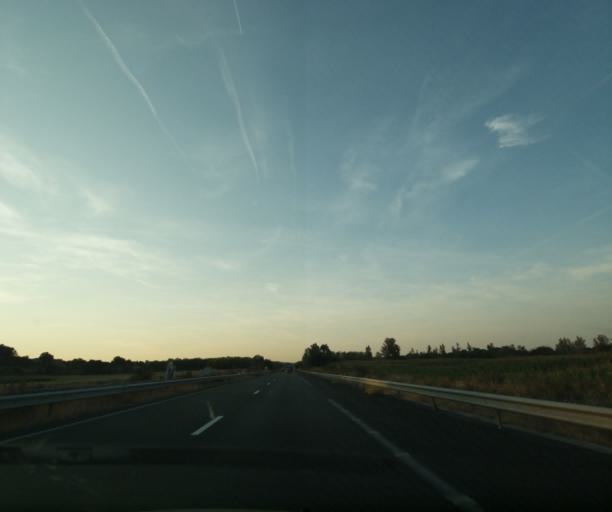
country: FR
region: Aquitaine
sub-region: Departement du Lot-et-Garonne
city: Damazan
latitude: 44.2734
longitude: 0.2746
